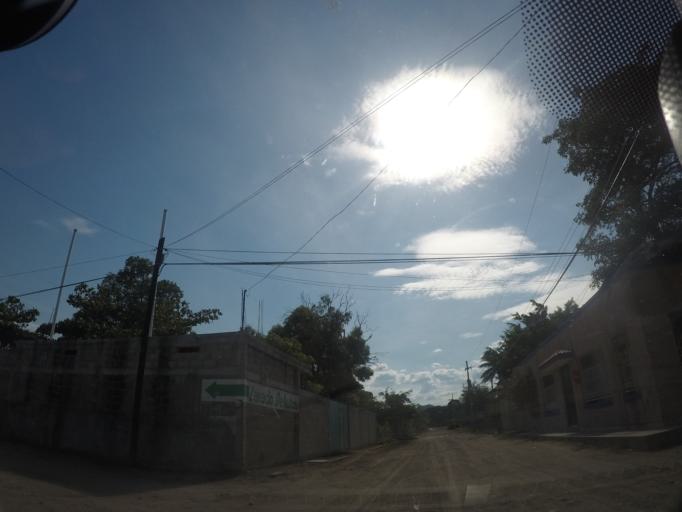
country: MX
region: Oaxaca
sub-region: Salina Cruz
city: Salina Cruz
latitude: 16.2163
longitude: -95.1994
